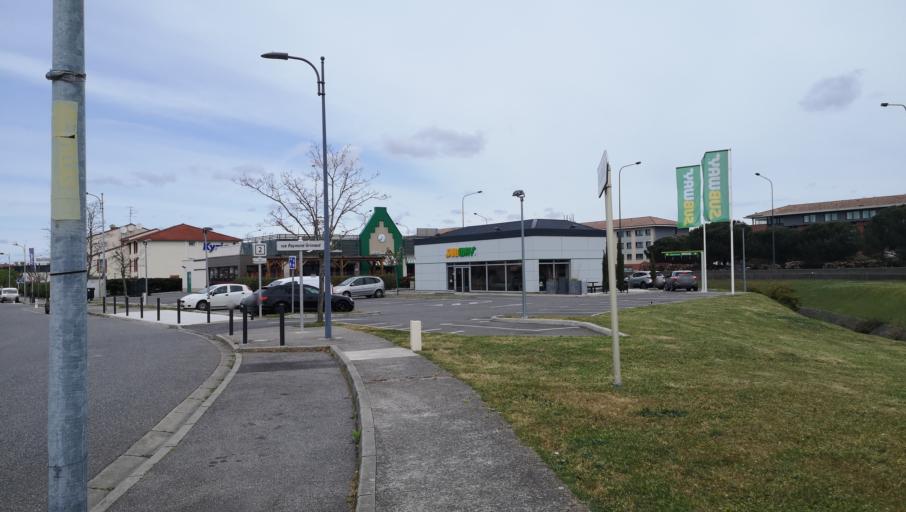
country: FR
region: Midi-Pyrenees
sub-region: Departement de la Haute-Garonne
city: Blagnac
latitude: 43.6381
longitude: 1.3756
